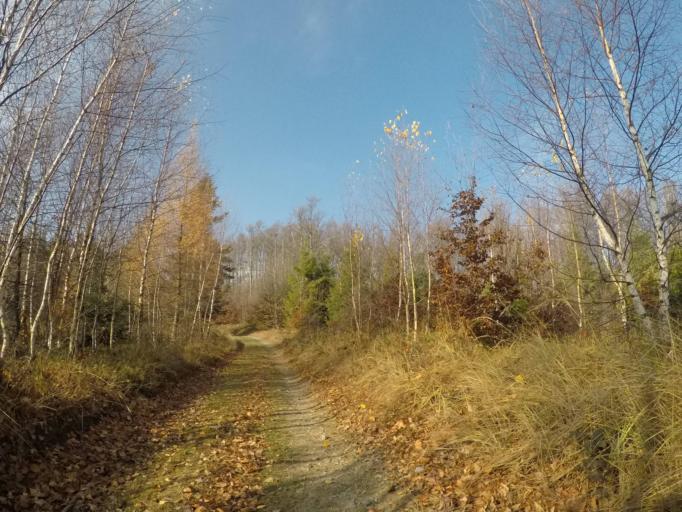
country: SK
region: Kosicky
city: Gelnica
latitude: 48.7653
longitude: 21.0620
